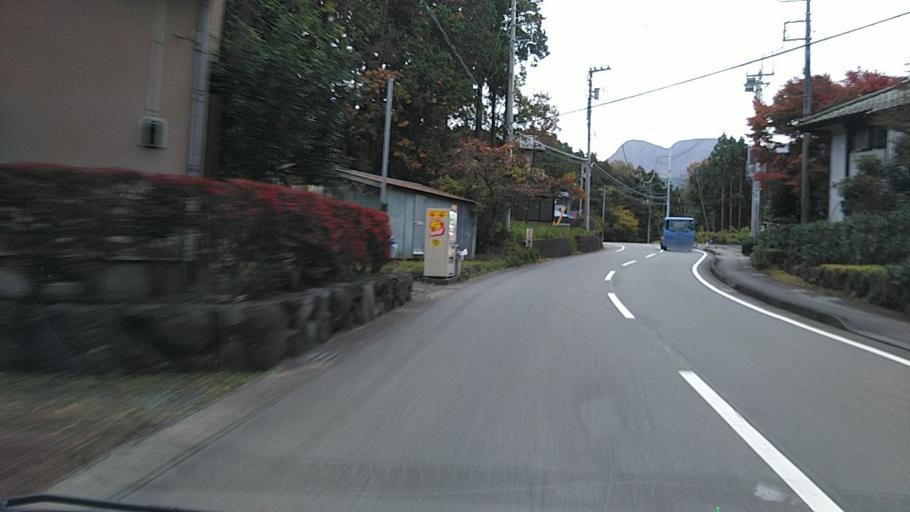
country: JP
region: Shizuoka
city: Gotemba
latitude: 35.3180
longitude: 138.9631
